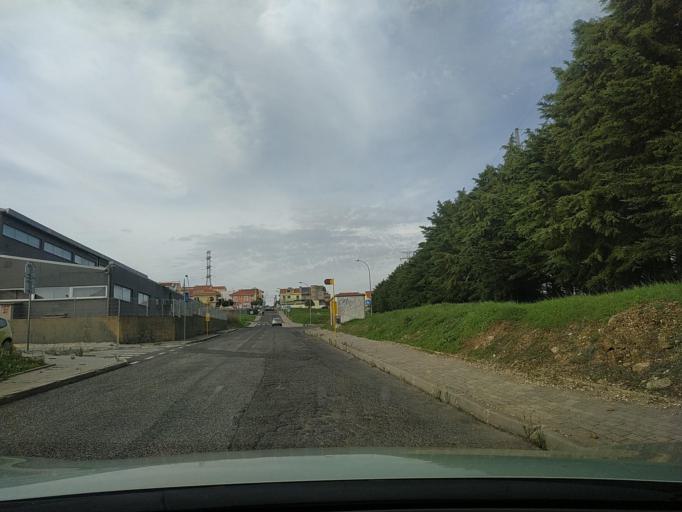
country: PT
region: Lisbon
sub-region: Sintra
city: Belas
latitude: 38.7766
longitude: -9.2399
